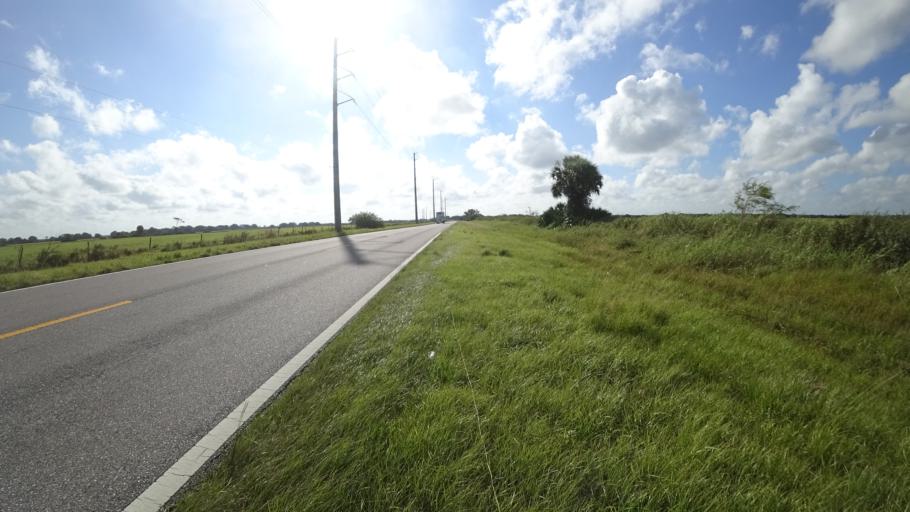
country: US
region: Florida
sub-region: Hillsborough County
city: Wimauma
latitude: 27.5193
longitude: -82.3276
